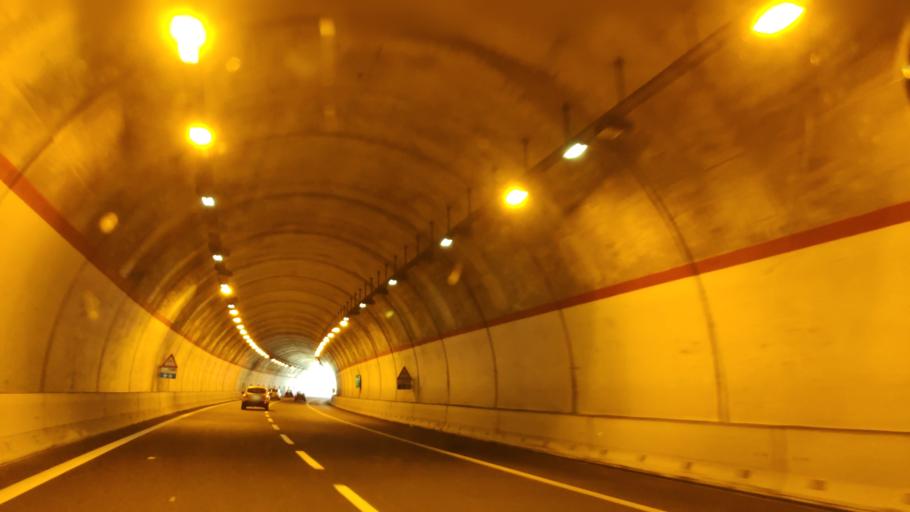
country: IT
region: Basilicate
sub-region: Provincia di Potenza
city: Nemoli
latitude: 40.0934
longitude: 15.8246
